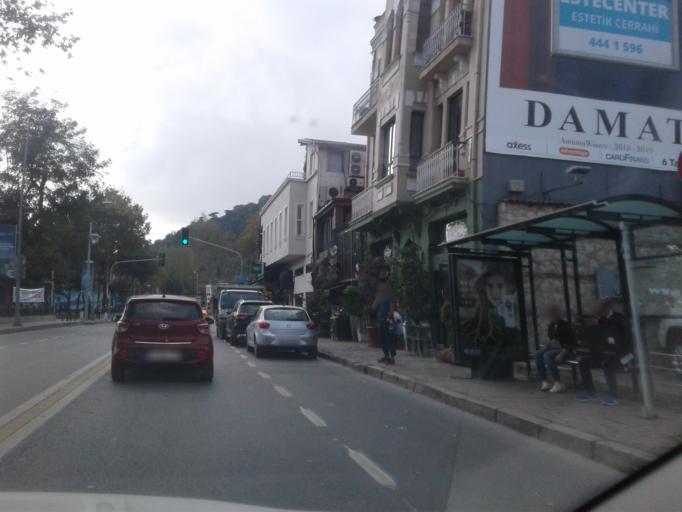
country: TR
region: Istanbul
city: UEskuedar
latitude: 41.0604
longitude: 29.0368
